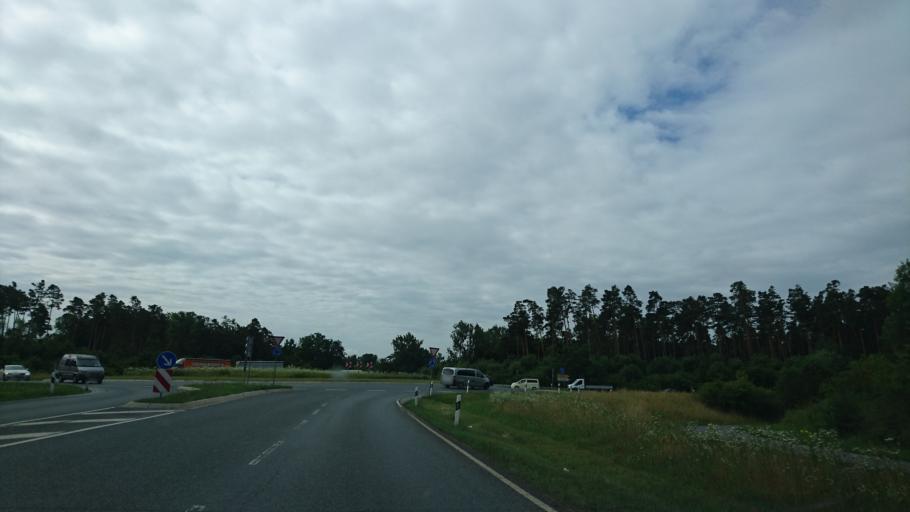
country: DE
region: Bavaria
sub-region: Regierungsbezirk Mittelfranken
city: Allersberg
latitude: 49.2484
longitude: 11.2120
